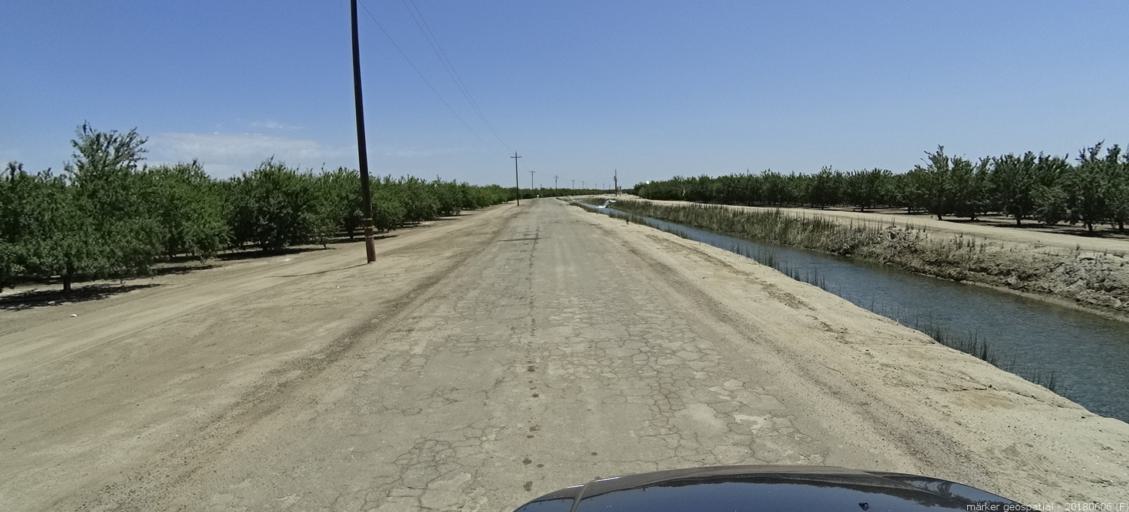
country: US
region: California
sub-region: Fresno County
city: Mendota
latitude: 36.7900
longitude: -120.3173
